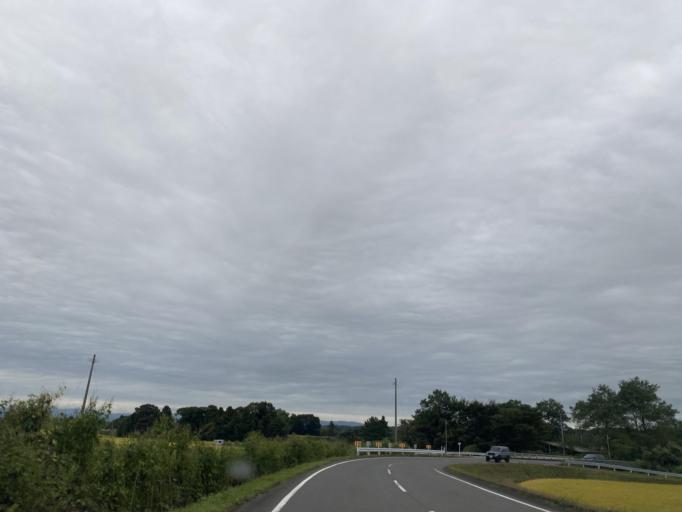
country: JP
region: Fukushima
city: Koriyama
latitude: 37.3452
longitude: 140.2653
